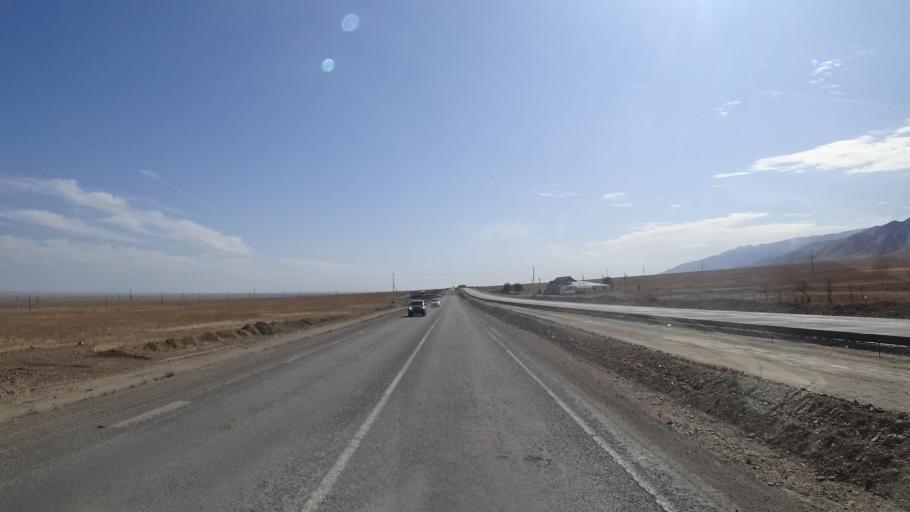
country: KG
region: Chuy
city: Ivanovka
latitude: 43.3853
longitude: 75.1656
